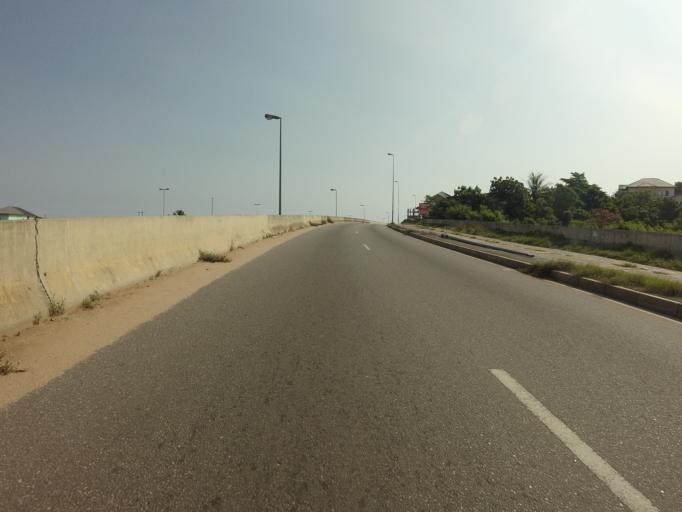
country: GH
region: Greater Accra
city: Gbawe
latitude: 5.6175
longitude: -0.2946
